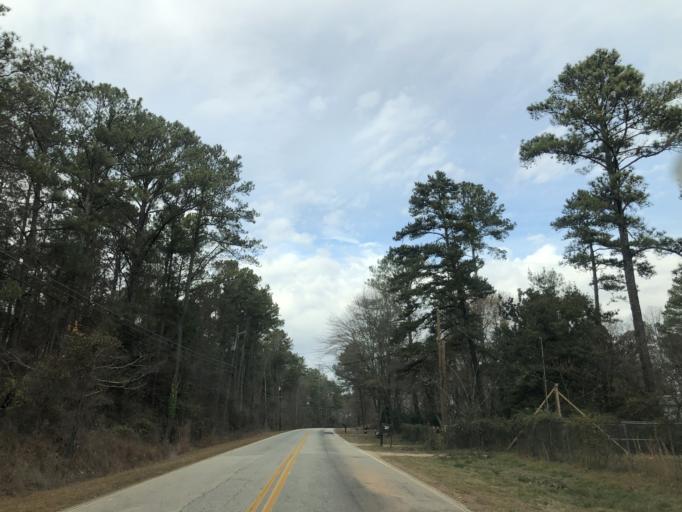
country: US
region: Georgia
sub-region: DeKalb County
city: Pine Mountain
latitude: 33.6646
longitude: -84.1798
